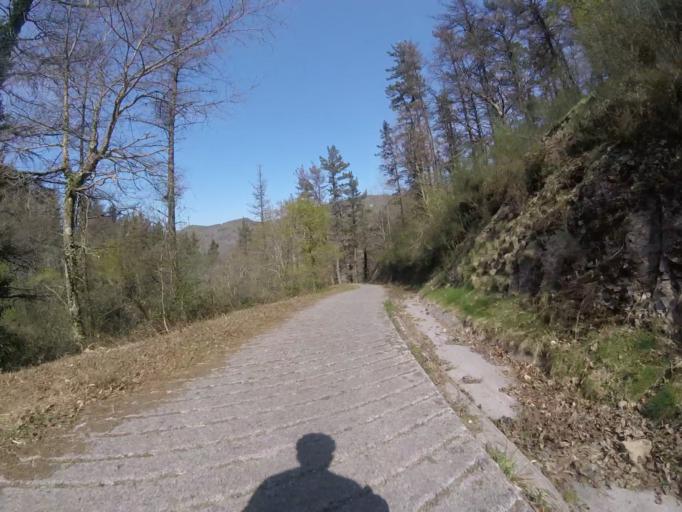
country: ES
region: Basque Country
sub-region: Provincia de Guipuzcoa
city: Irun
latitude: 43.2760
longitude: -1.8073
